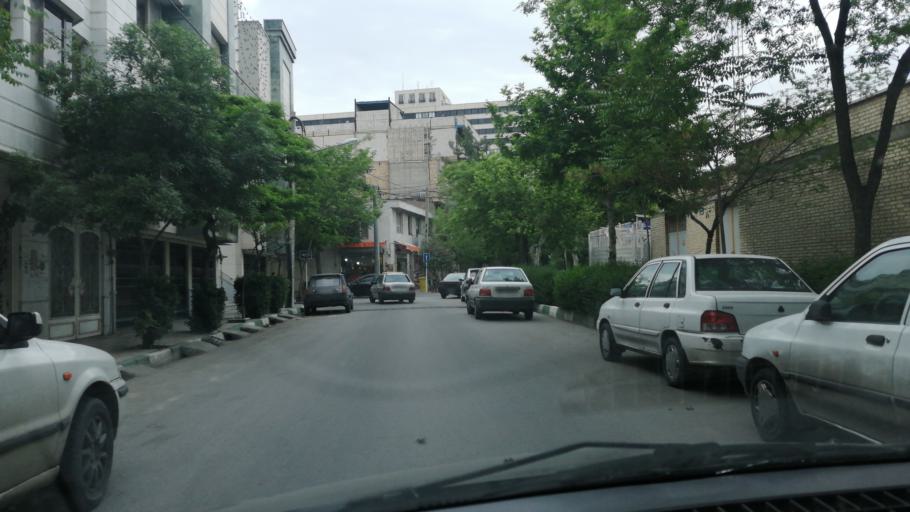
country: IR
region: Razavi Khorasan
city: Mashhad
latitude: 36.2881
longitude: 59.5864
